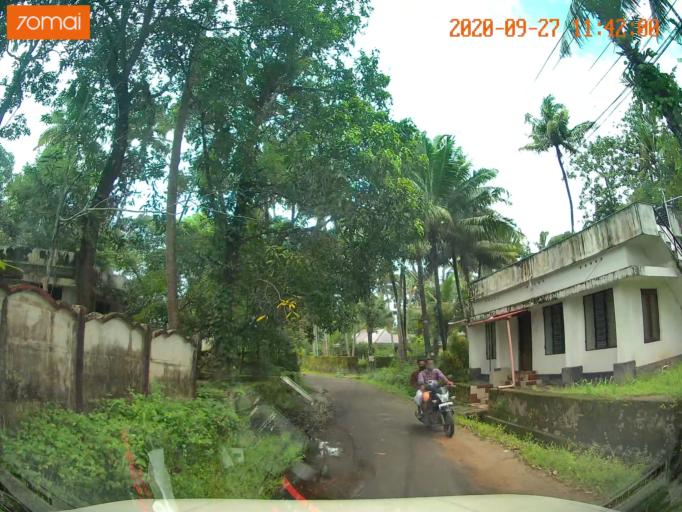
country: IN
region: Kerala
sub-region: Thrissur District
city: Thanniyam
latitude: 10.4715
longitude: 76.1140
